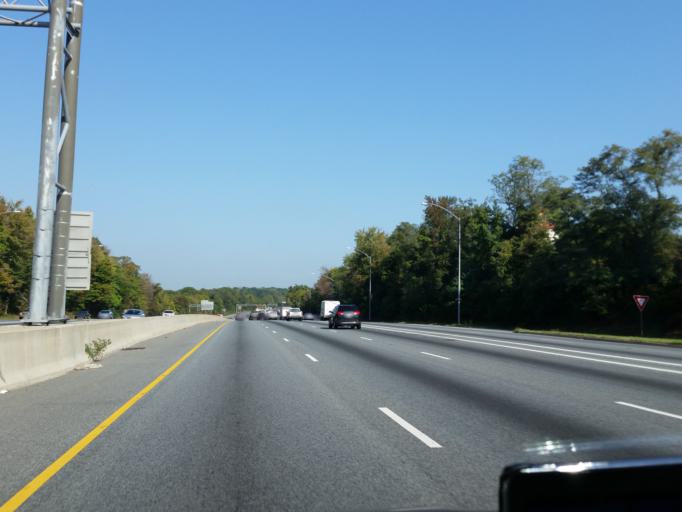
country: US
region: Maryland
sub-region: Prince George's County
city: Glenarden
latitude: 38.9199
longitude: -76.8524
